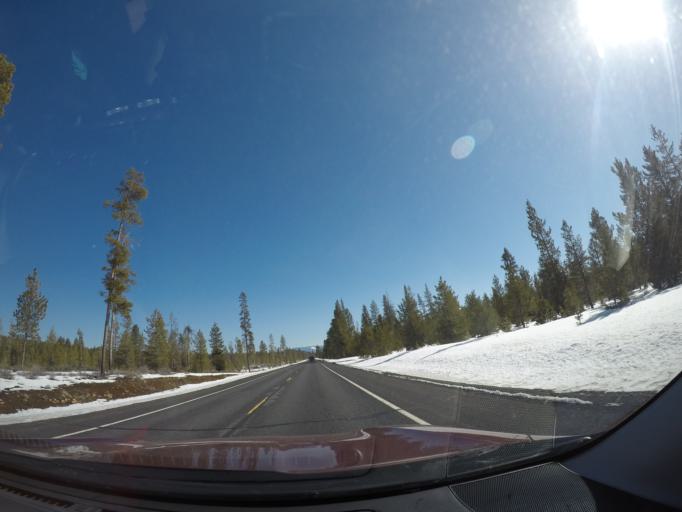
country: US
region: Oregon
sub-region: Deschutes County
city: Three Rivers
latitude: 43.8657
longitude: -121.5402
